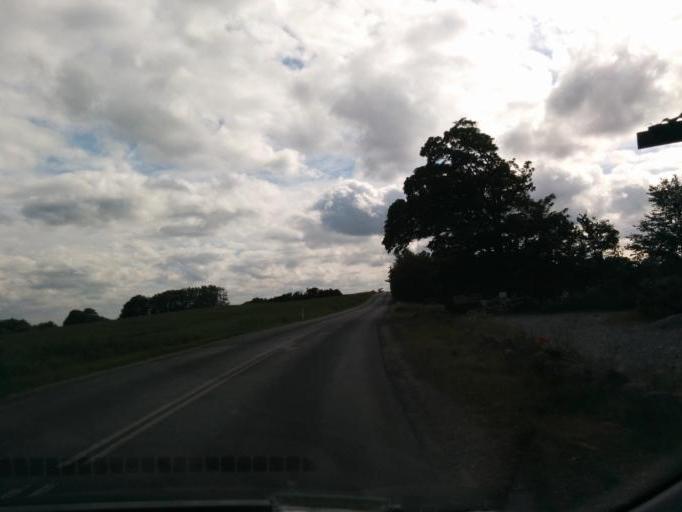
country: DK
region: Central Jutland
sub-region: Syddjurs Kommune
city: Ronde
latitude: 56.3198
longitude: 10.4297
